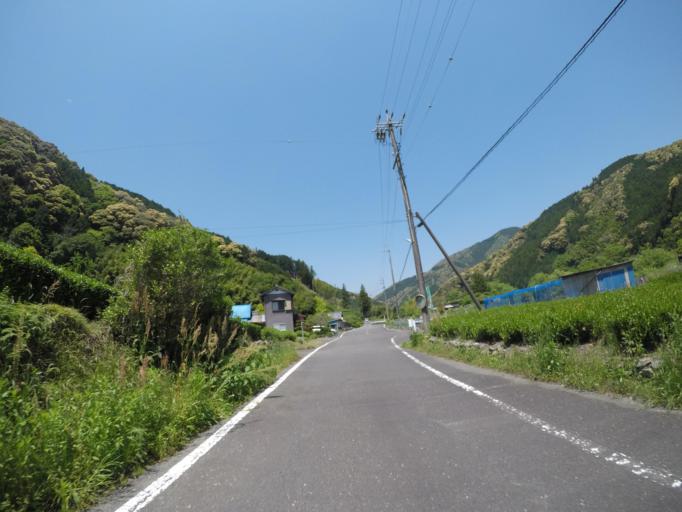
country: JP
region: Shizuoka
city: Shizuoka-shi
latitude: 35.0101
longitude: 138.2722
